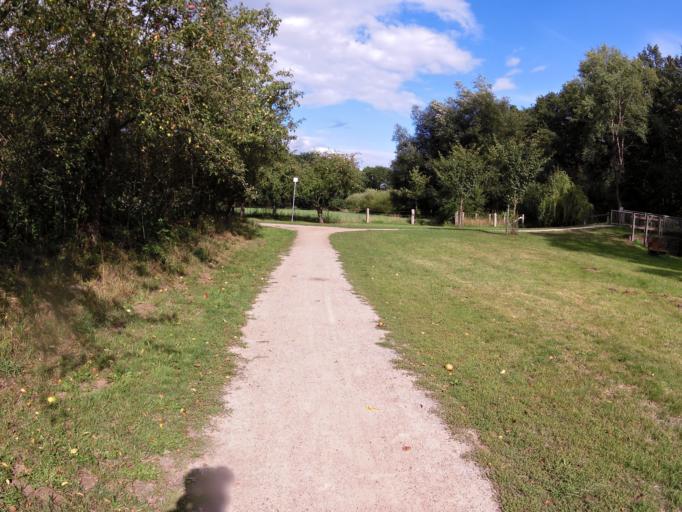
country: DE
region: Lower Saxony
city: Hamersen
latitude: 53.2769
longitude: 9.4738
